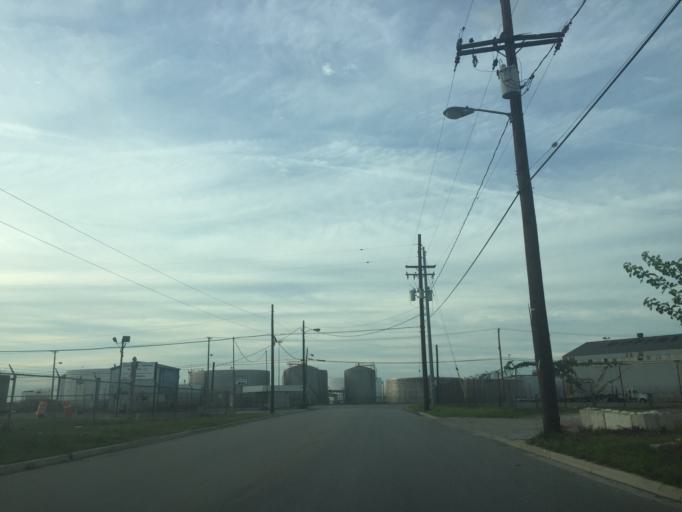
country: US
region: Maryland
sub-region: Anne Arundel County
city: Brooklyn Park
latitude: 39.2407
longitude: -76.5764
